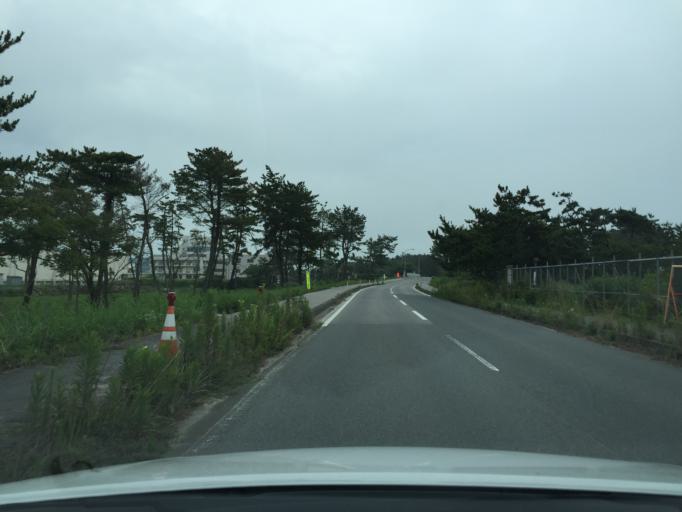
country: JP
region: Fukushima
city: Iwaki
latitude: 37.0215
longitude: 140.9711
